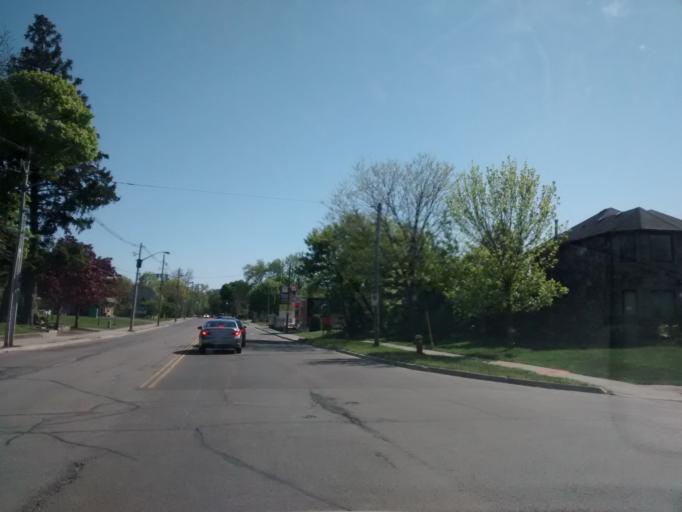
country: CA
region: Ontario
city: Oakville
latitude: 43.3913
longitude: -79.7146
